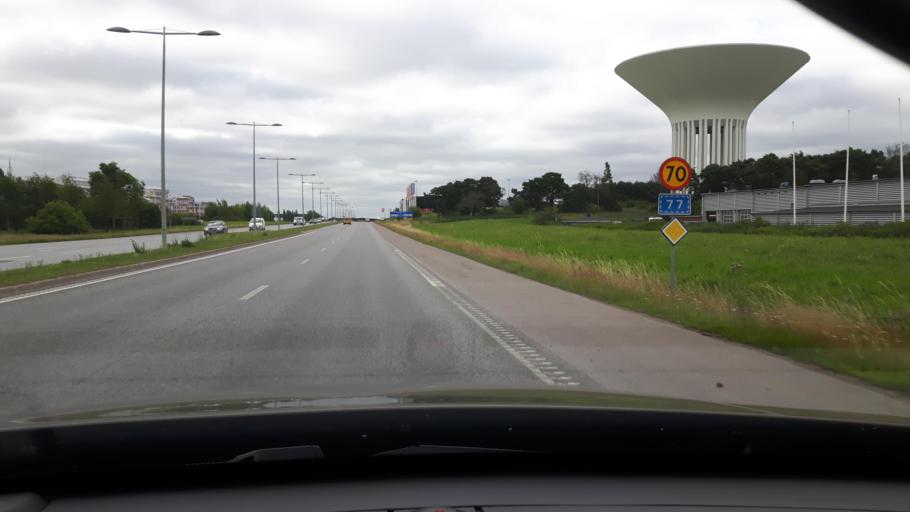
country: SE
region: Uppsala
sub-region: Uppsala Kommun
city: Uppsala
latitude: 59.8581
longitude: 17.6788
